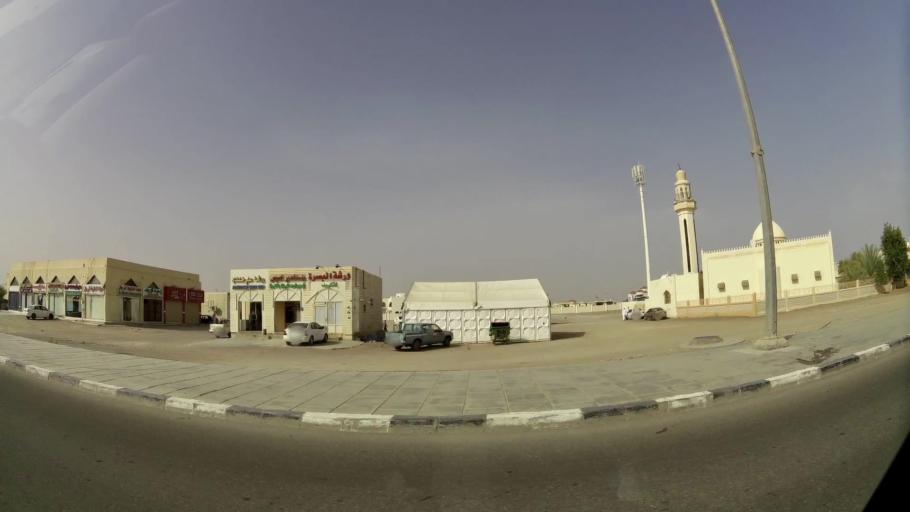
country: AE
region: Abu Dhabi
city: Al Ain
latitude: 24.2110
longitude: 55.5858
